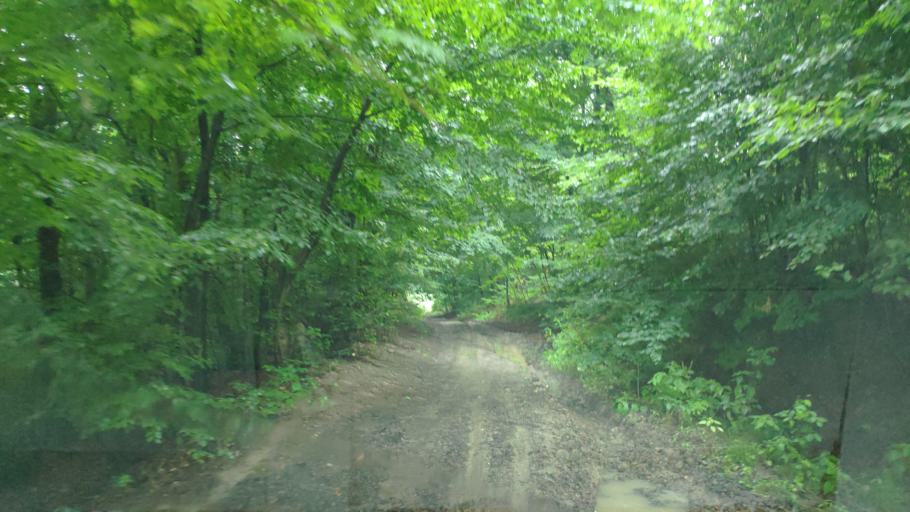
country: SK
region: Presovsky
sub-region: Okres Presov
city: Presov
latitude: 48.8653
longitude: 21.1951
